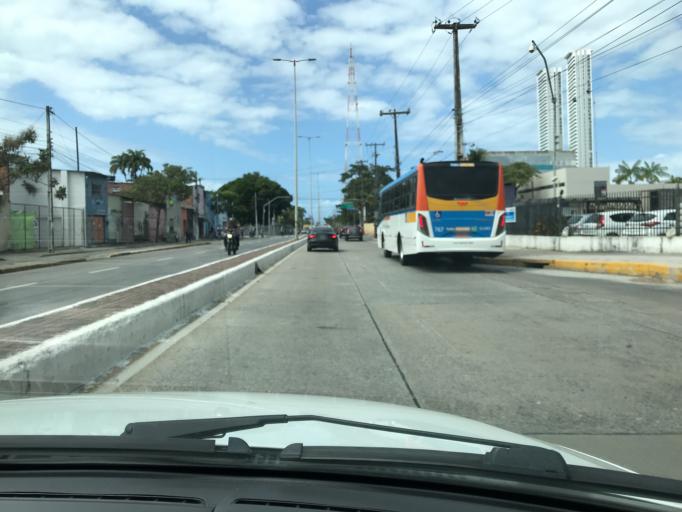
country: BR
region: Pernambuco
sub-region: Recife
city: Recife
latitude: -8.0468
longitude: -34.8779
